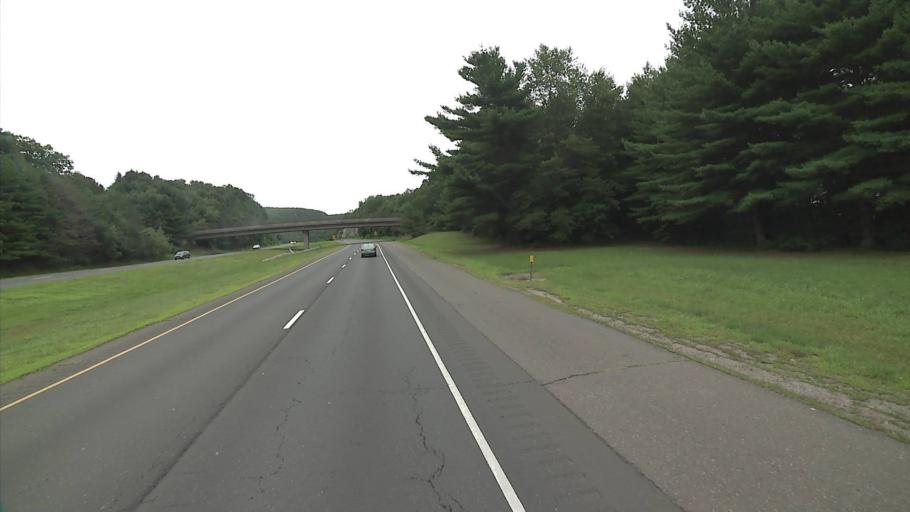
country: US
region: Connecticut
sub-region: New Haven County
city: Seymour
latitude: 41.4381
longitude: -73.0670
